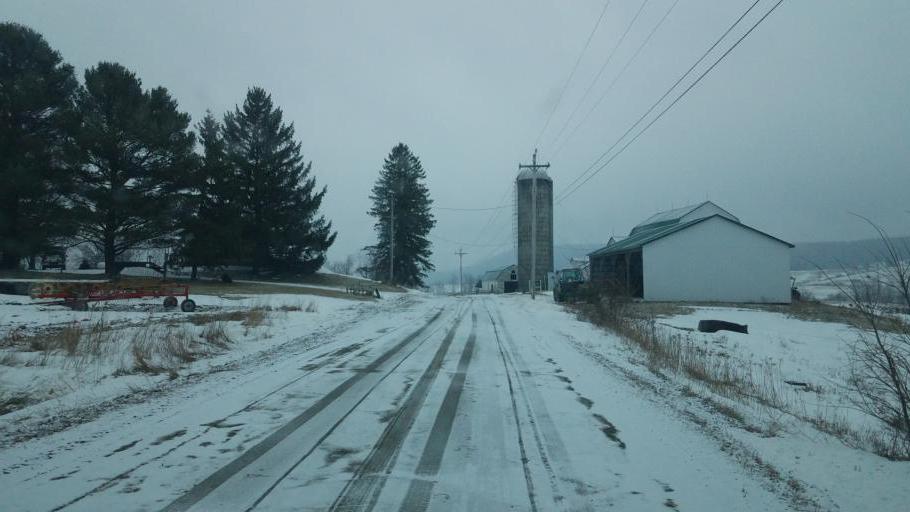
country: US
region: Pennsylvania
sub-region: Tioga County
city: Elkland
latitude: 42.1047
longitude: -77.4694
